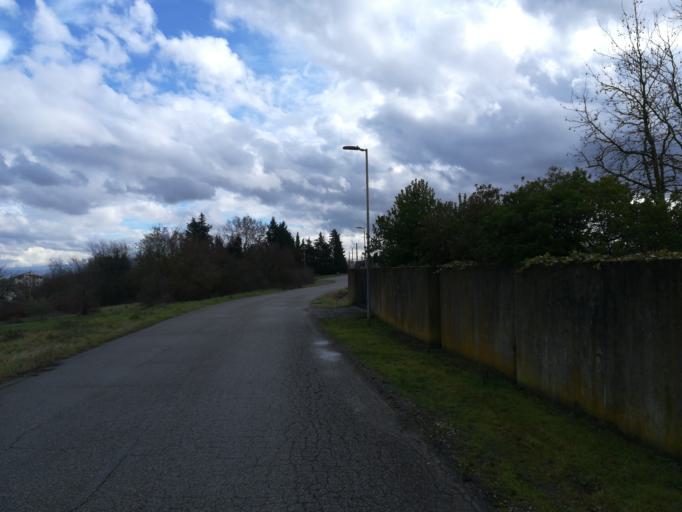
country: IT
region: Tuscany
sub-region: Provincia di Prato
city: Poggio A Caiano
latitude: 43.8077
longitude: 11.0476
